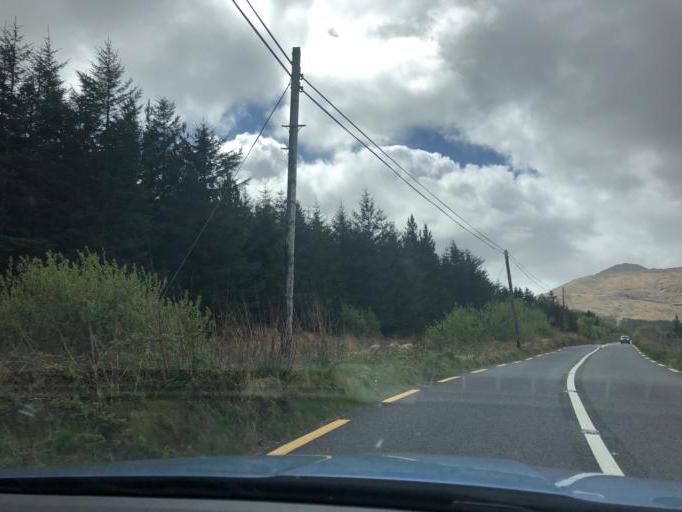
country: IE
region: Munster
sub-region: Ciarrai
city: Cahersiveen
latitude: 51.8256
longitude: -9.9662
